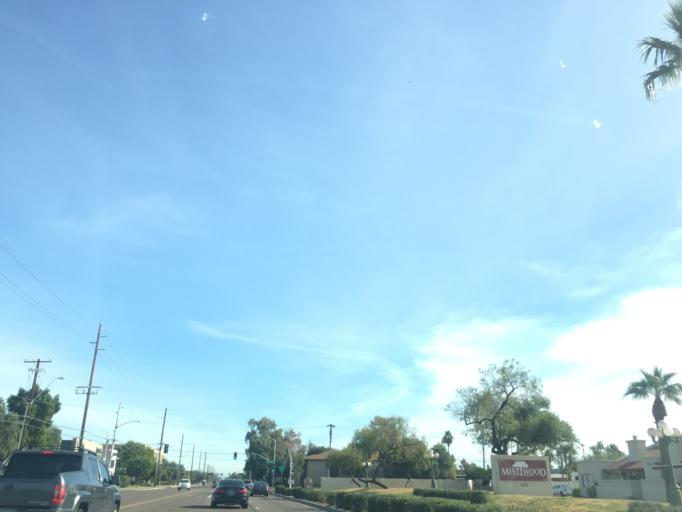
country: US
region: Arizona
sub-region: Maricopa County
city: Tempe Junction
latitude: 33.3928
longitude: -111.9491
